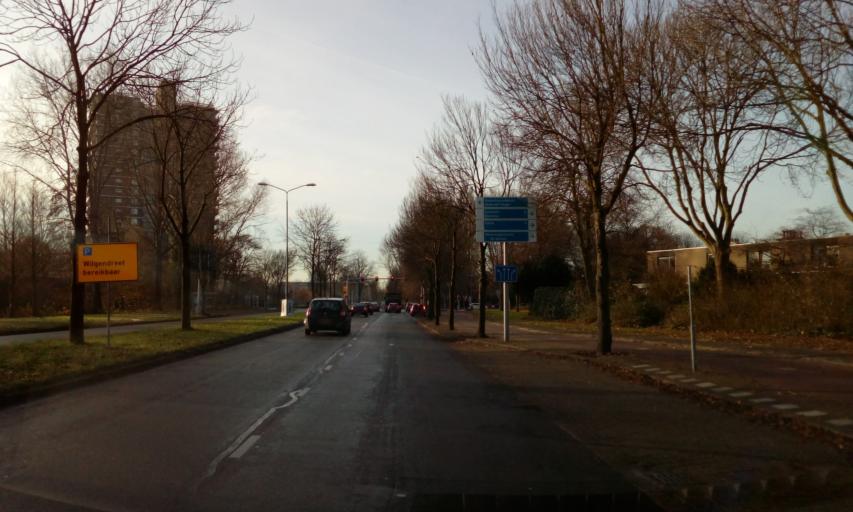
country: NL
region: South Holland
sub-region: Gemeente Leidschendam-Voorburg
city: Voorburg
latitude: 52.0839
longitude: 4.3763
